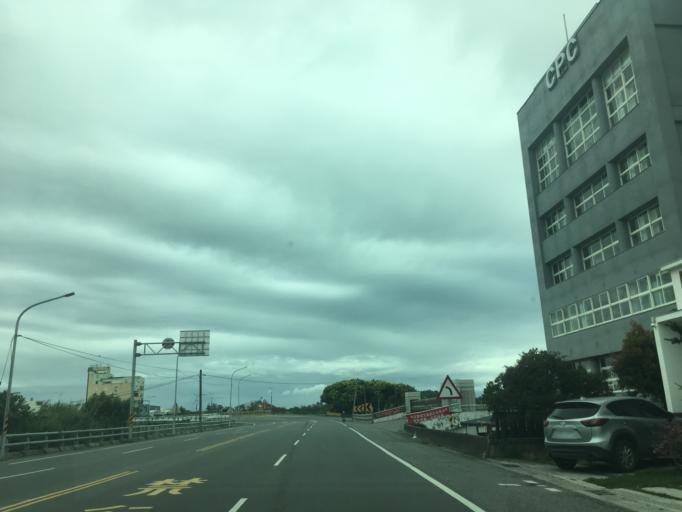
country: TW
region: Taiwan
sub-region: Taitung
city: Taitung
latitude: 22.7665
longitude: 121.1309
